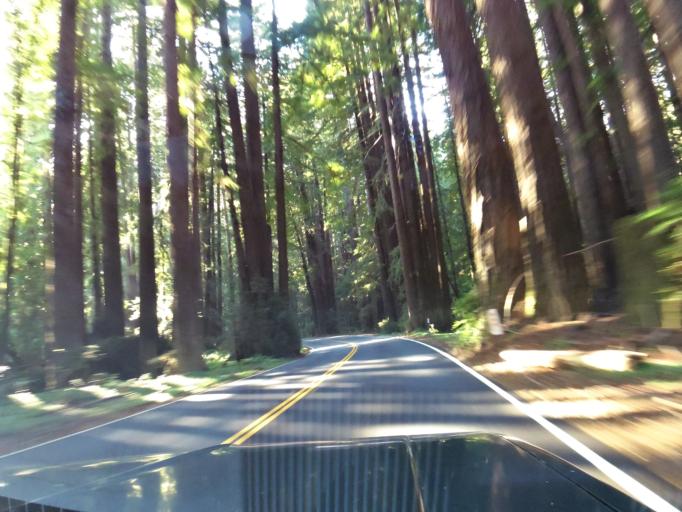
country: US
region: California
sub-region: Mendocino County
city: Boonville
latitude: 39.1654
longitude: -123.6406
